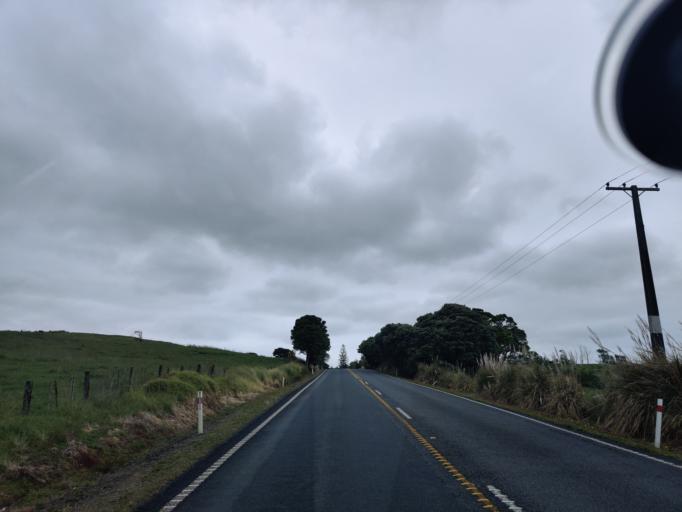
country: NZ
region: Northland
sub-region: Kaipara District
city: Dargaville
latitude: -36.1256
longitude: 174.1152
